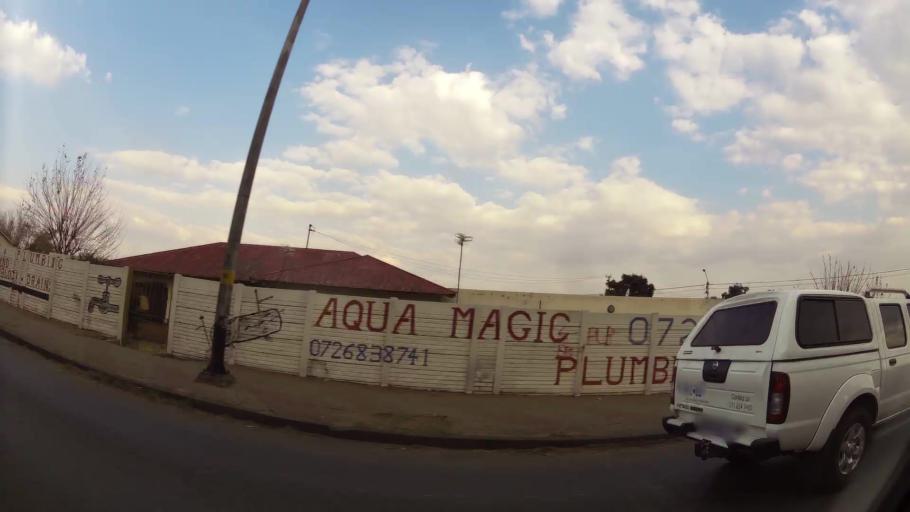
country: ZA
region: Gauteng
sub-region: Ekurhuleni Metropolitan Municipality
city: Germiston
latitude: -26.2437
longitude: 28.1916
